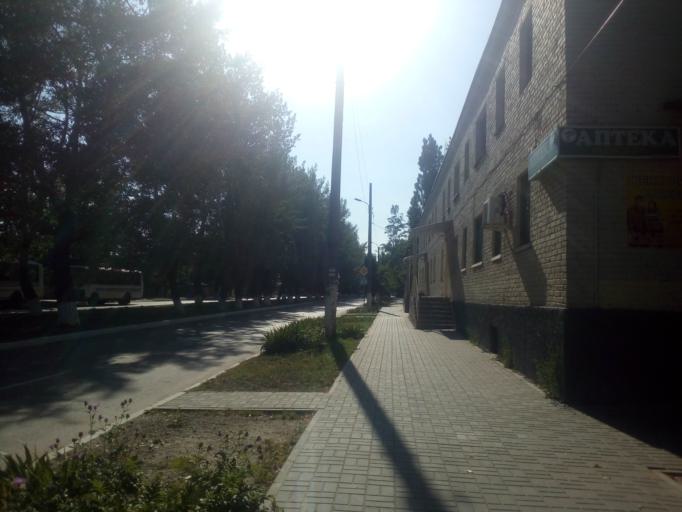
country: RU
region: Rostov
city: Sholokhovskiy
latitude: 48.2819
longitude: 41.0543
